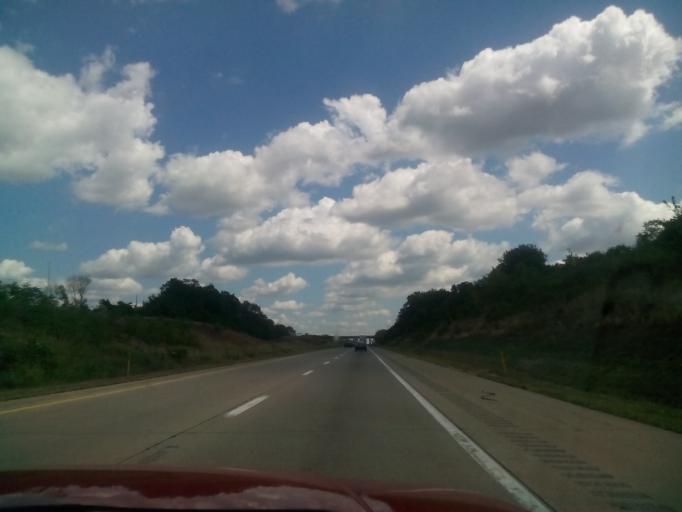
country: US
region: Pennsylvania
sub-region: Northumberland County
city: Riverside
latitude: 40.9862
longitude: -76.7123
